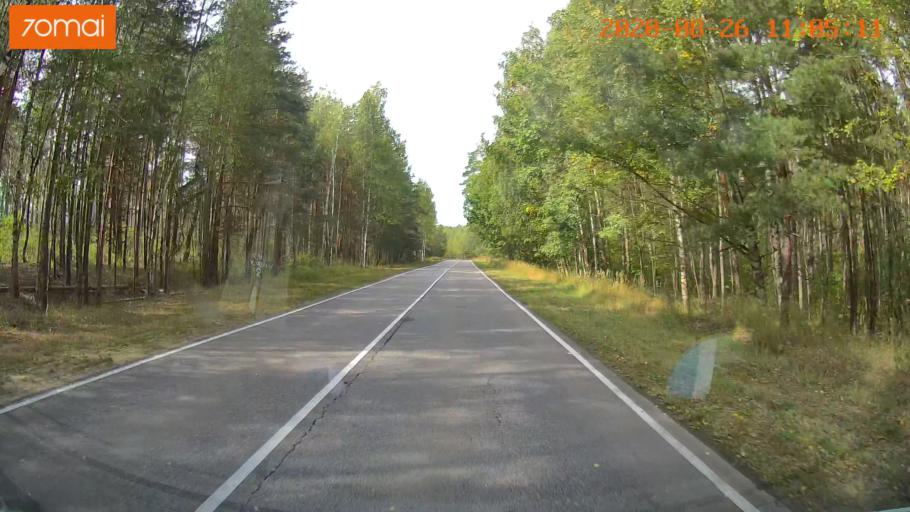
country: RU
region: Rjazan
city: Izhevskoye
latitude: 54.5288
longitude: 41.1788
